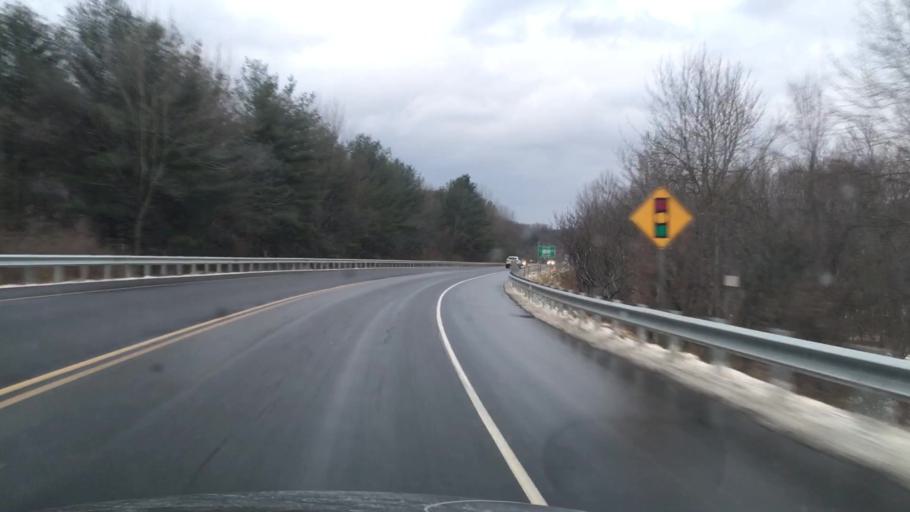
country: US
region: New Hampshire
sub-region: Sullivan County
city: Claremont
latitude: 43.4020
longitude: -72.3959
